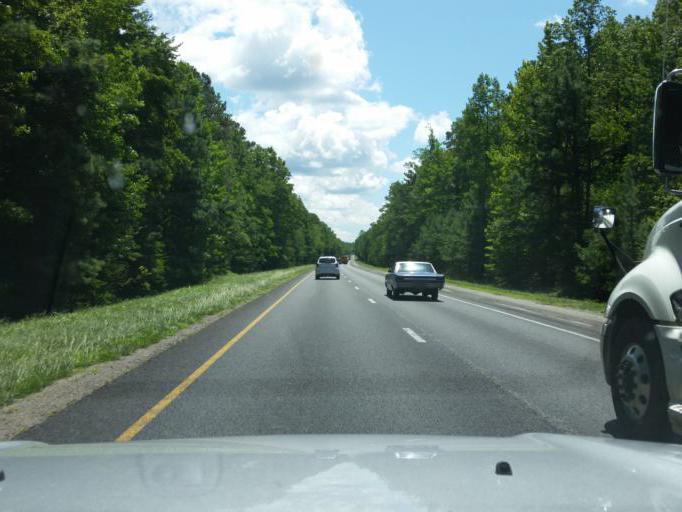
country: US
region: Virginia
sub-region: New Kent County
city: New Kent
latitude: 37.4731
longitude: -76.9072
